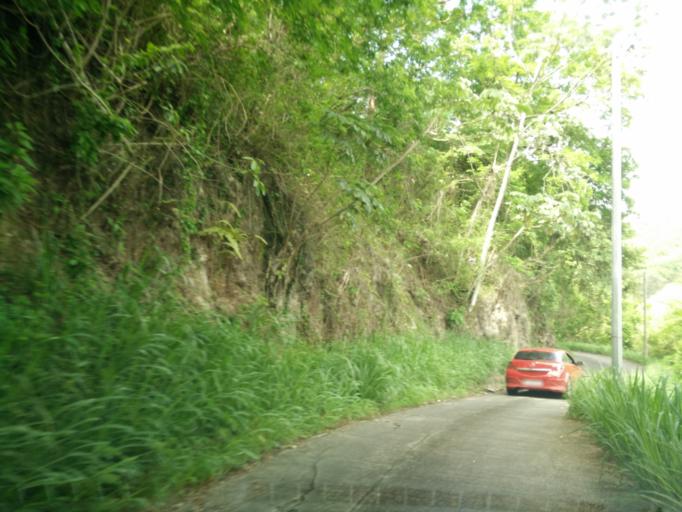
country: MQ
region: Martinique
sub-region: Martinique
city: Saint-Pierre
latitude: 14.7176
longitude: -61.1652
